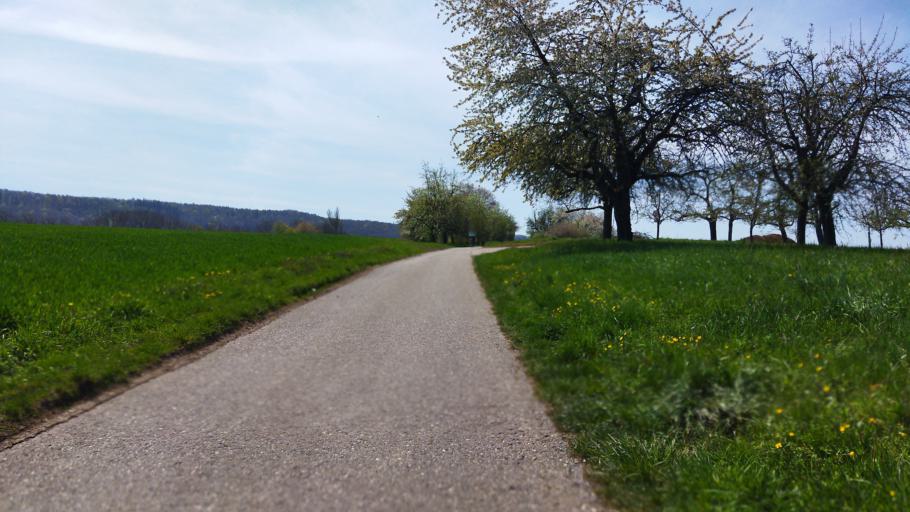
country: DE
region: Baden-Wuerttemberg
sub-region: Regierungsbezirk Stuttgart
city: Pfaffenhofen
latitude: 49.0553
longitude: 8.9691
